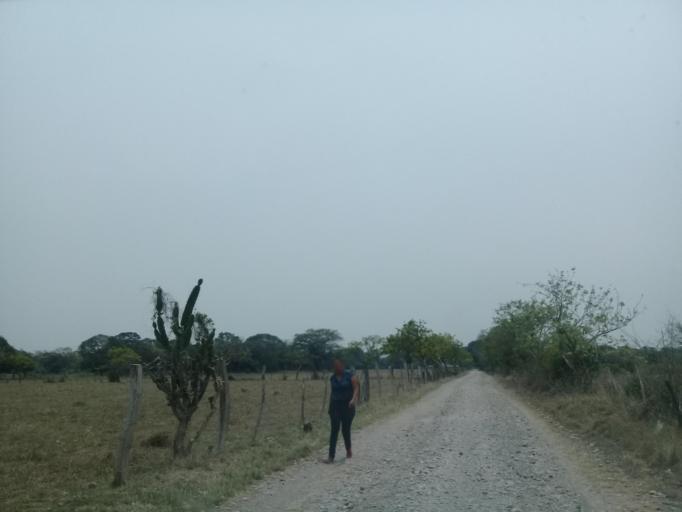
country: MX
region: Veracruz
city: Jamapa
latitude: 18.9333
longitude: -96.2064
